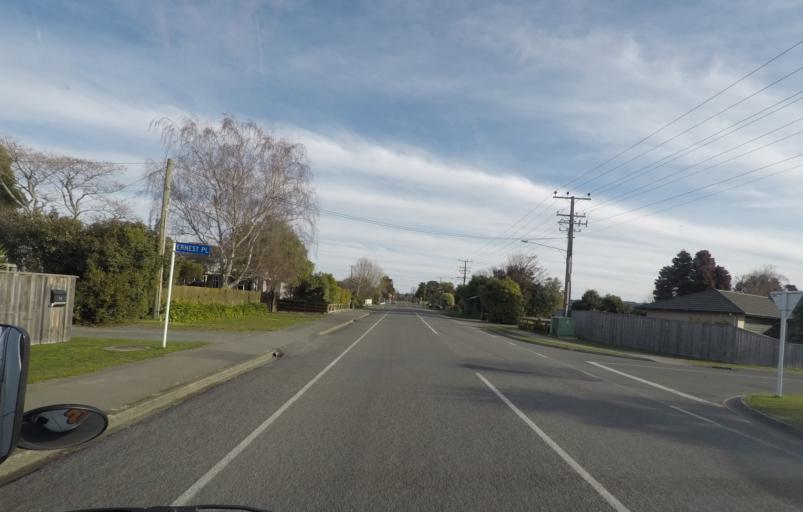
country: NZ
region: Tasman
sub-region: Tasman District
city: Brightwater
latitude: -41.3763
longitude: 173.1037
